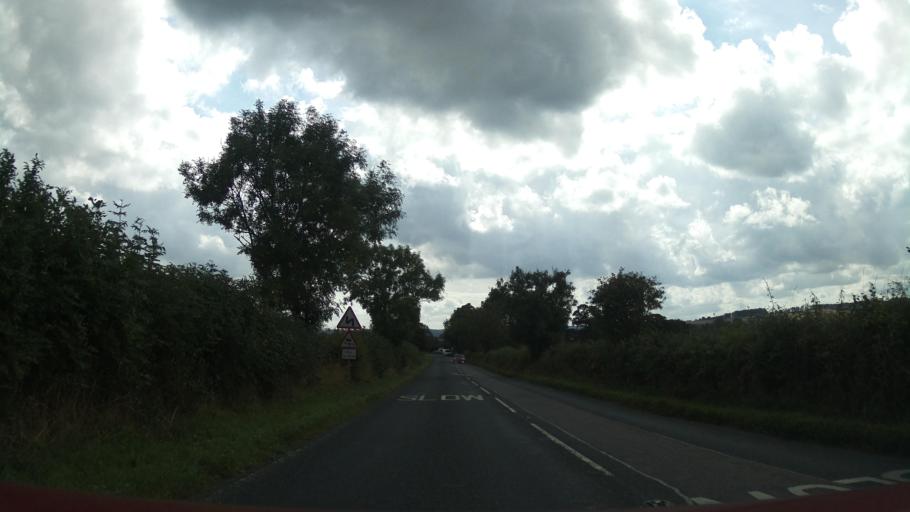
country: GB
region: England
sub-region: North Yorkshire
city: Catterick Garrison
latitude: 54.4274
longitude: -1.6822
